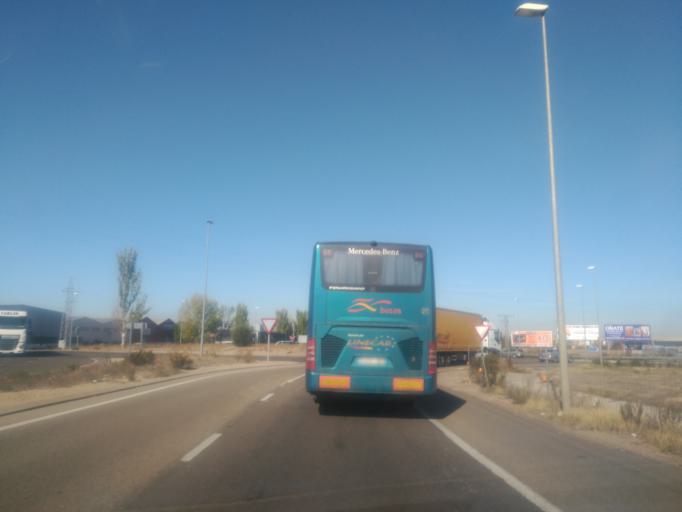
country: ES
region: Castille and Leon
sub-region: Provincia de Valladolid
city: Cisterniga
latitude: 41.6214
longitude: -4.6949
